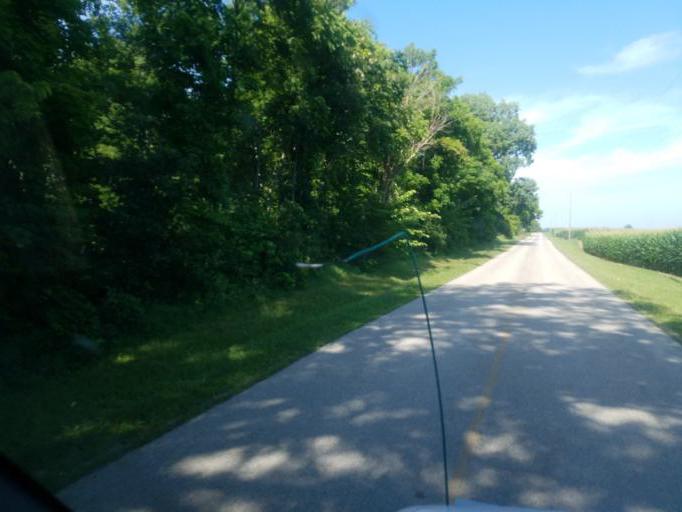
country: US
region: Ohio
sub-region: Logan County
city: Northwood
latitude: 40.5531
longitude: -83.6626
